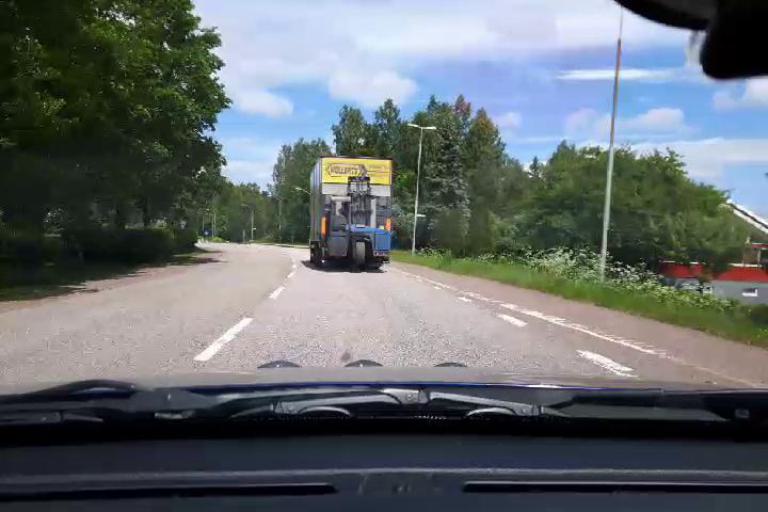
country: SE
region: Uppsala
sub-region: Osthammars Kommun
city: Bjorklinge
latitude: 60.0894
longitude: 17.5545
